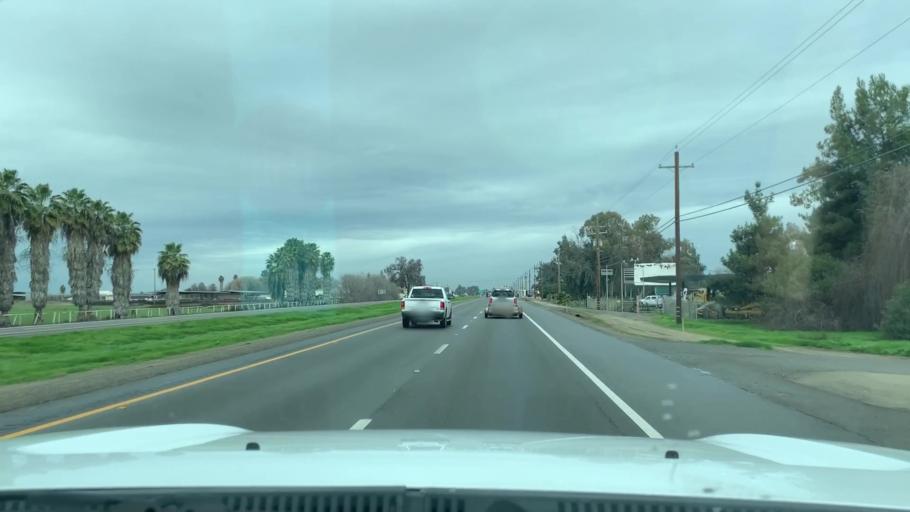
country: US
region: California
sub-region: Kings County
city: Lemoore
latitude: 36.3353
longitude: -119.8079
